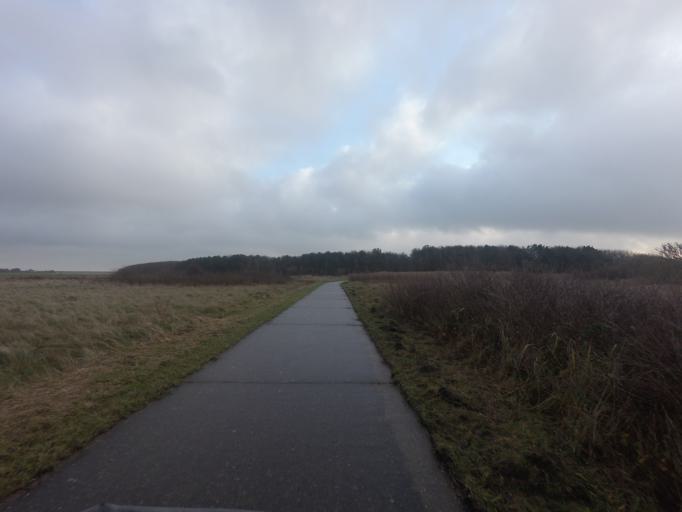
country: NL
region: North Holland
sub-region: Gemeente Texel
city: Den Burg
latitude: 53.1668
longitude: 4.8463
